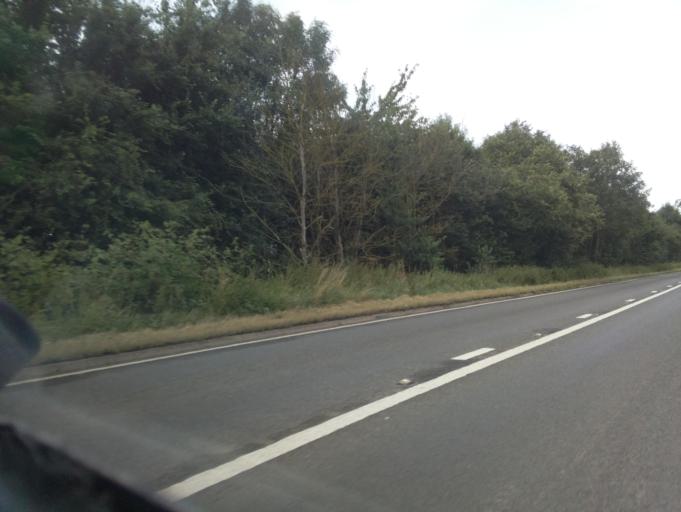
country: GB
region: England
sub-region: Warwickshire
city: Southam
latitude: 52.2707
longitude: -1.3700
